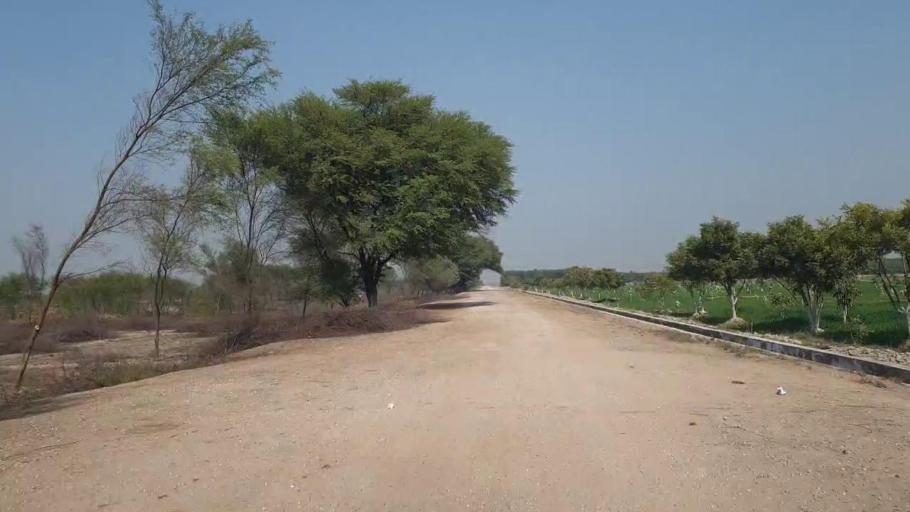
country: PK
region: Sindh
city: Mirwah Gorchani
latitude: 25.3547
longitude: 68.9316
